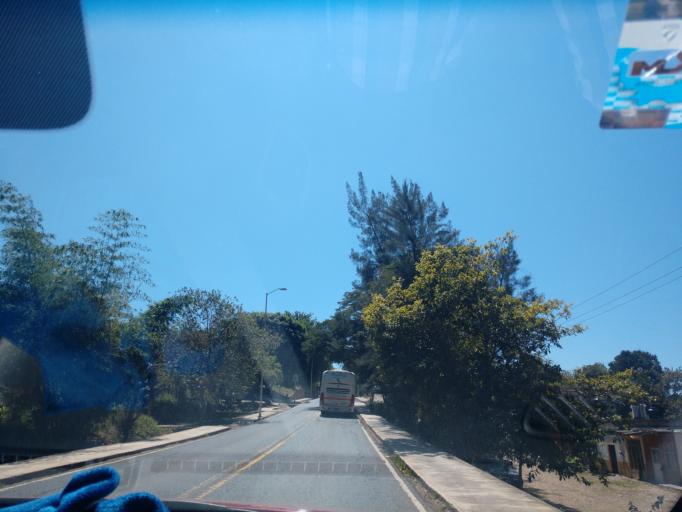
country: MX
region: Nayarit
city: Compostela
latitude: 21.2480
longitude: -104.9014
